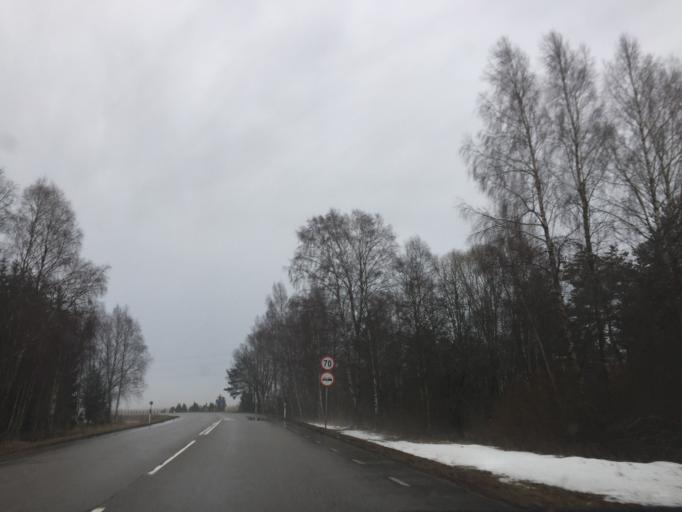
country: EE
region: Saare
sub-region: Orissaare vald
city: Orissaare
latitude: 58.5488
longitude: 23.1223
